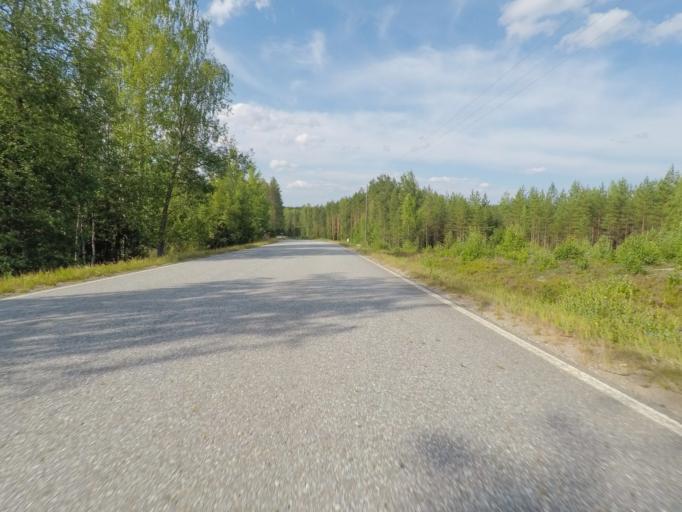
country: FI
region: Southern Savonia
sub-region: Savonlinna
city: Sulkava
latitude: 61.7160
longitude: 28.2100
